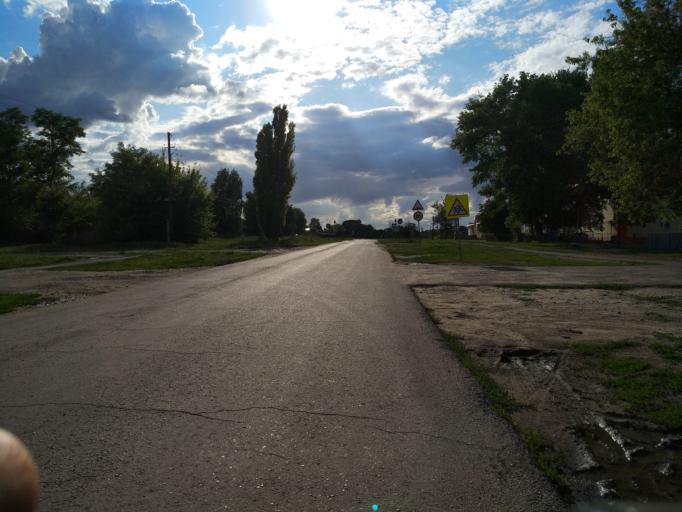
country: RU
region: Lipetsk
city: Dobrinka
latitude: 52.0380
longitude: 40.5462
